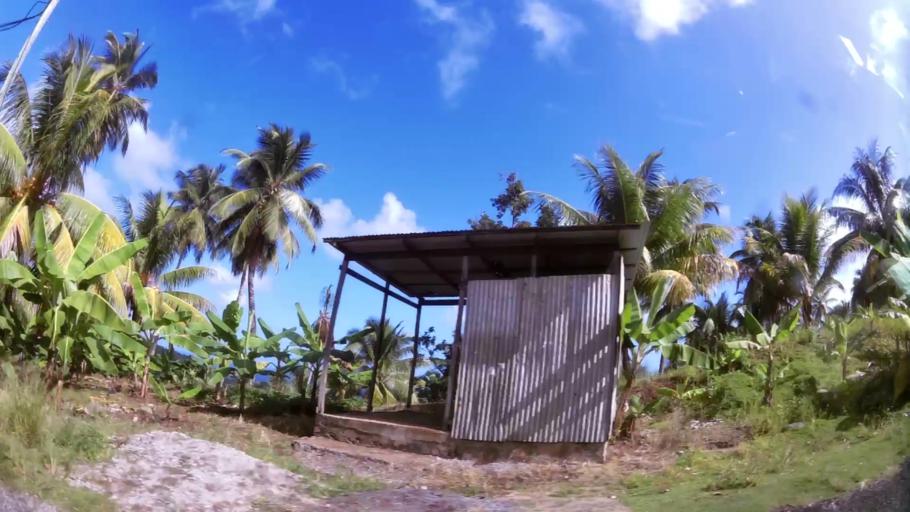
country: DM
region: Saint David
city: Castle Bruce
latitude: 15.4728
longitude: -61.2474
